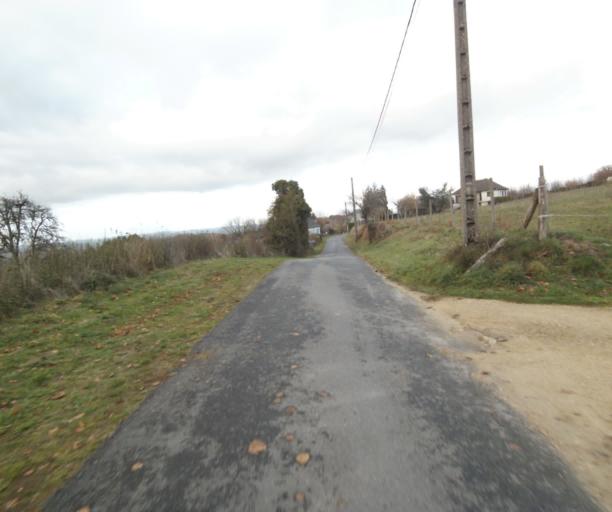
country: FR
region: Limousin
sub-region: Departement de la Correze
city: Sainte-Fortunade
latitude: 45.2060
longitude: 1.7780
